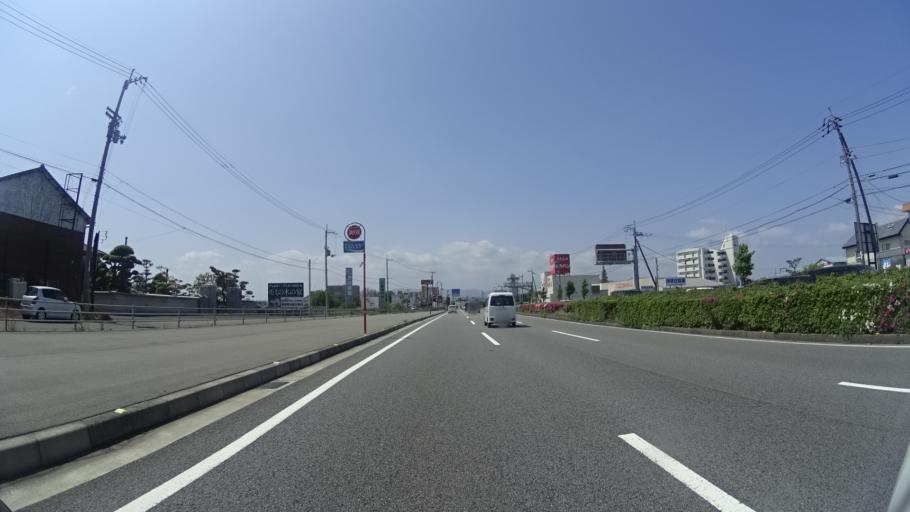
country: JP
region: Tokushima
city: Tokushima-shi
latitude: 34.0993
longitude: 134.5747
